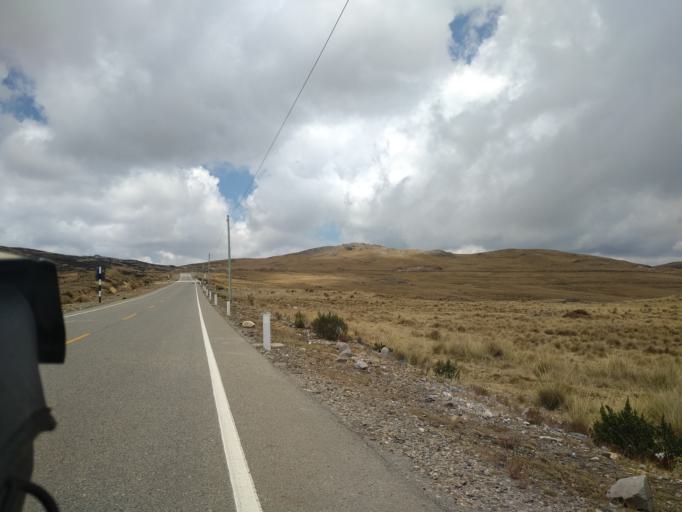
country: PE
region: La Libertad
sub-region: Provincia de Santiago de Chuco
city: Quiruvilca
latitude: -7.9448
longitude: -78.1900
